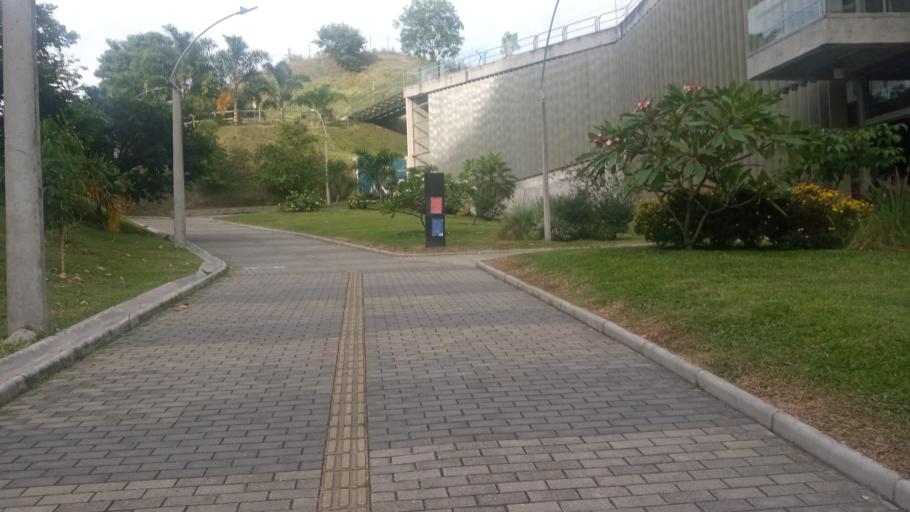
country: CO
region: Antioquia
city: Medellin
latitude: 6.2700
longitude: -75.5893
